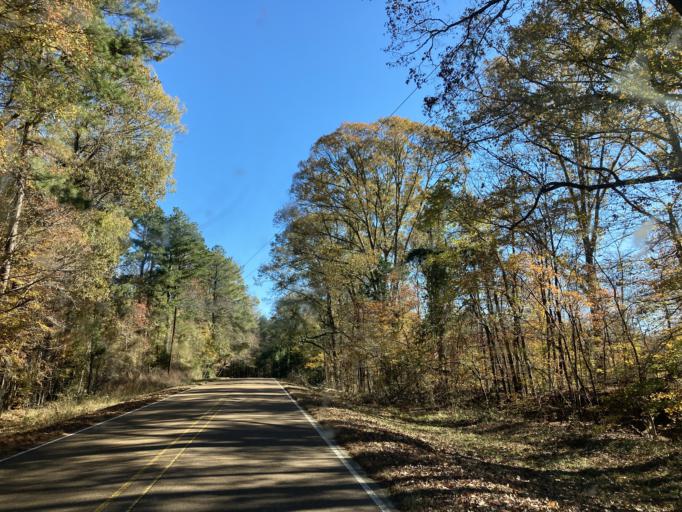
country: US
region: Mississippi
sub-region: Hinds County
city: Lynchburg
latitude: 32.5957
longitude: -90.5400
